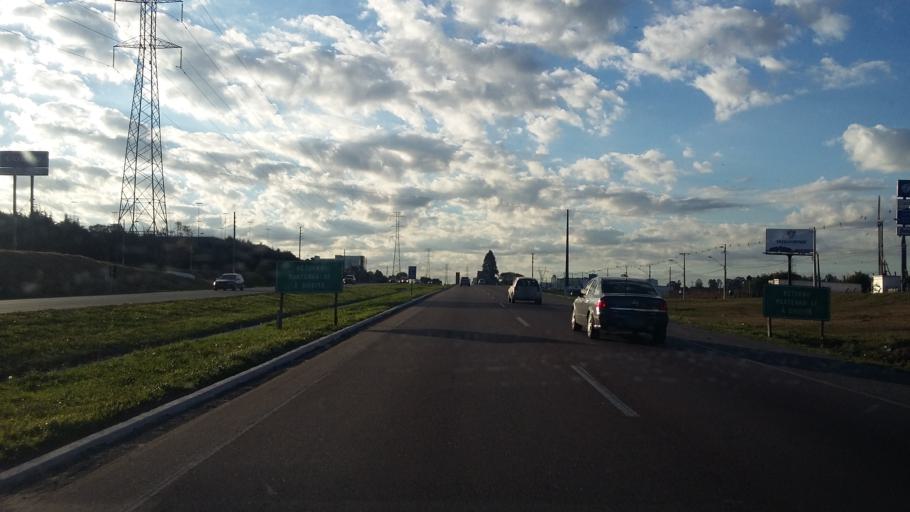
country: BR
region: Parana
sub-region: Curitiba
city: Curitiba
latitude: -25.4593
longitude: -49.3594
